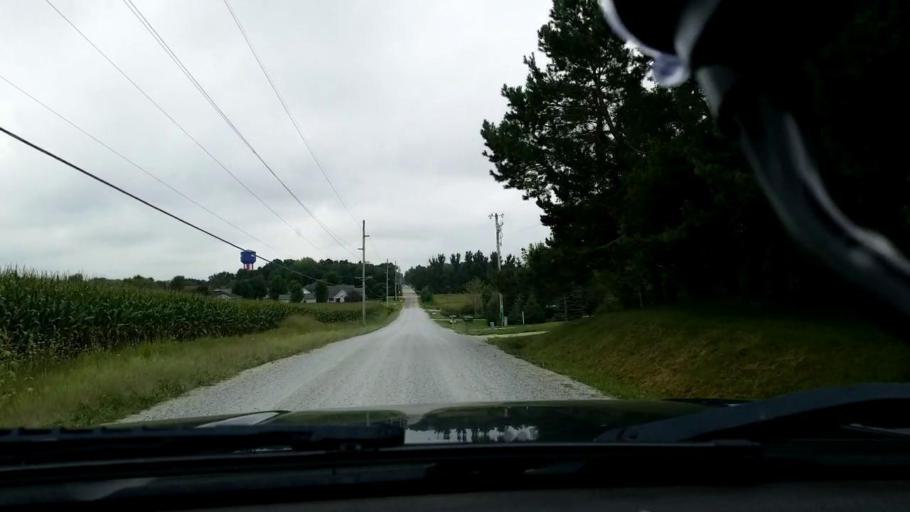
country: US
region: Iowa
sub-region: Buchanan County
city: Independence
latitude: 42.4869
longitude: -91.8846
